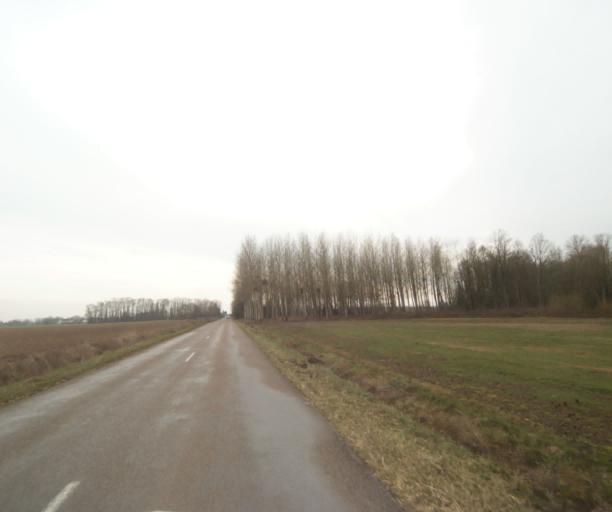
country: FR
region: Champagne-Ardenne
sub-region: Departement de la Haute-Marne
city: Villiers-en-Lieu
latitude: 48.6750
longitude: 4.8889
